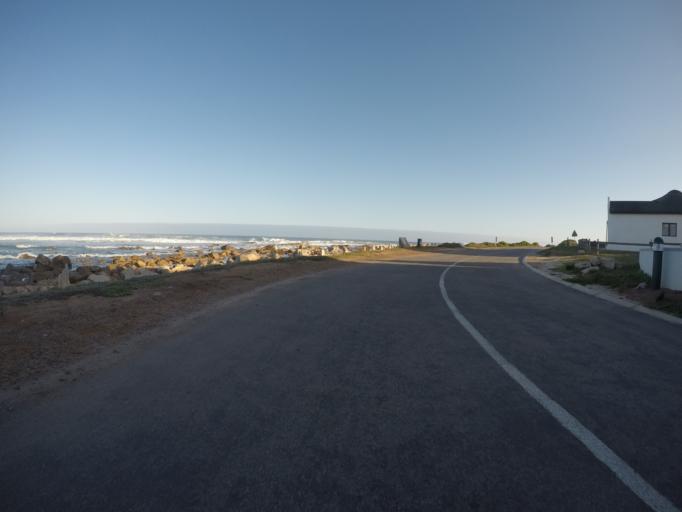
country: ZA
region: Western Cape
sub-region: Eden District Municipality
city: Riversdale
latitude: -34.4322
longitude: 21.3359
